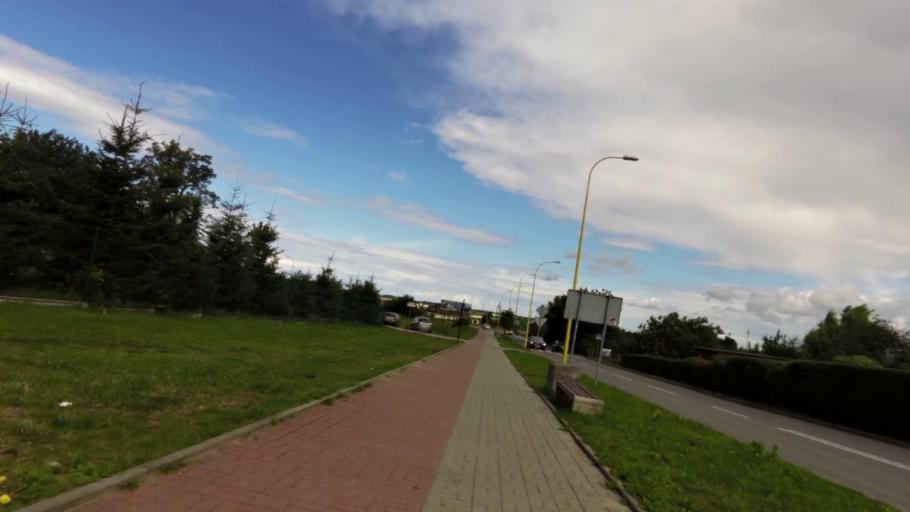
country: PL
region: West Pomeranian Voivodeship
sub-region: Powiat slawienski
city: Darlowo
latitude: 54.4267
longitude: 16.4168
